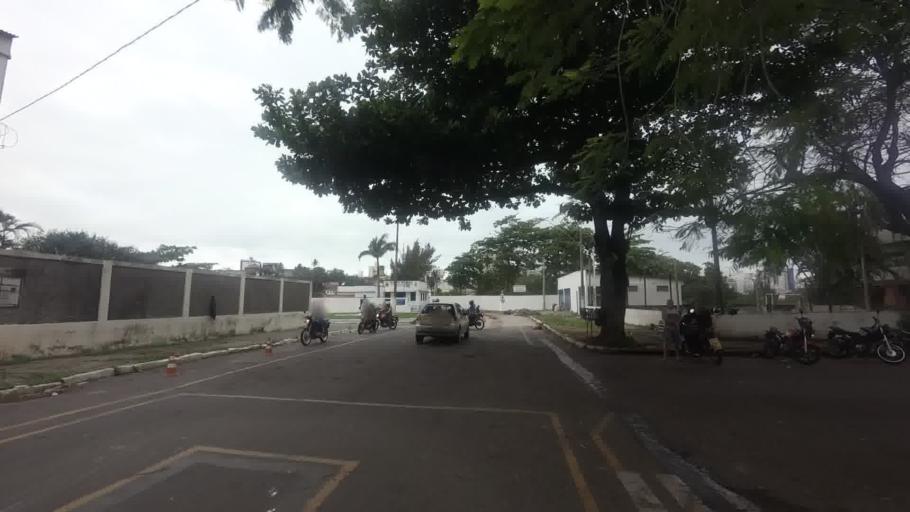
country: BR
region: Espirito Santo
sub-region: Guarapari
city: Guarapari
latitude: -20.6641
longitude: -40.4981
